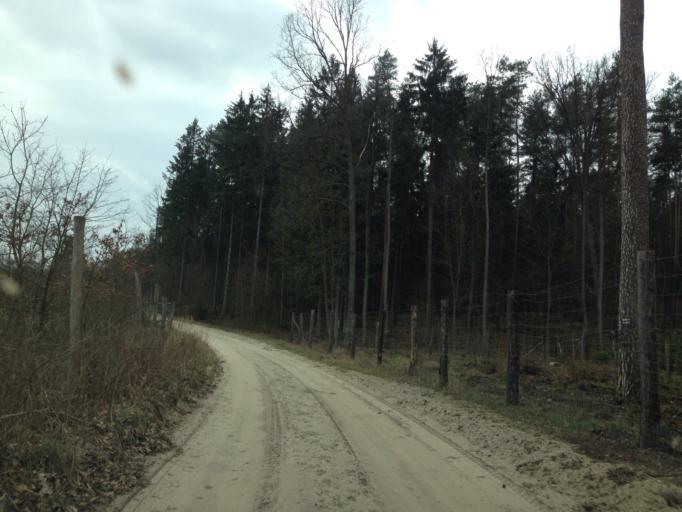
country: PL
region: Kujawsko-Pomorskie
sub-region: Powiat brodnicki
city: Gorzno
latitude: 53.2181
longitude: 19.7376
